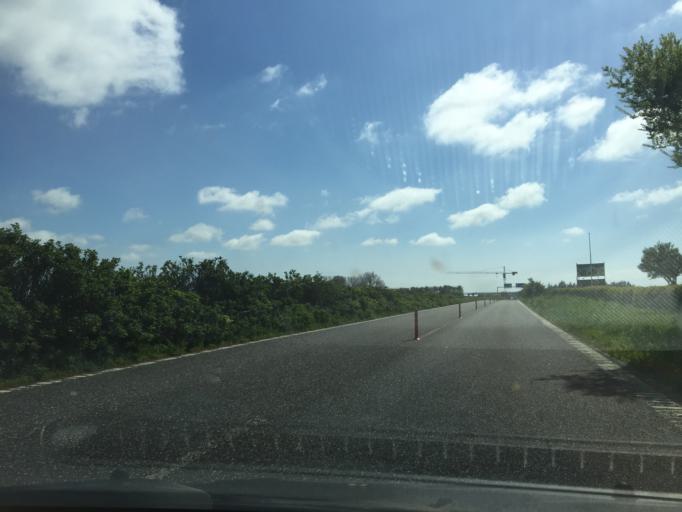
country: DK
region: Zealand
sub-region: Lolland Kommune
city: Holeby
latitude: 54.7216
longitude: 11.4329
